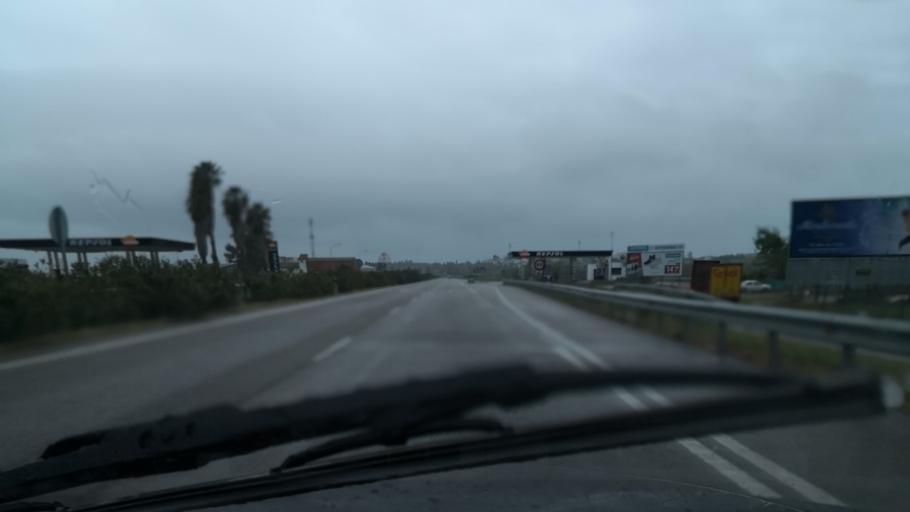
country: ES
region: Extremadura
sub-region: Provincia de Badajoz
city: Badajoz
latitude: 38.9074
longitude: -6.9653
